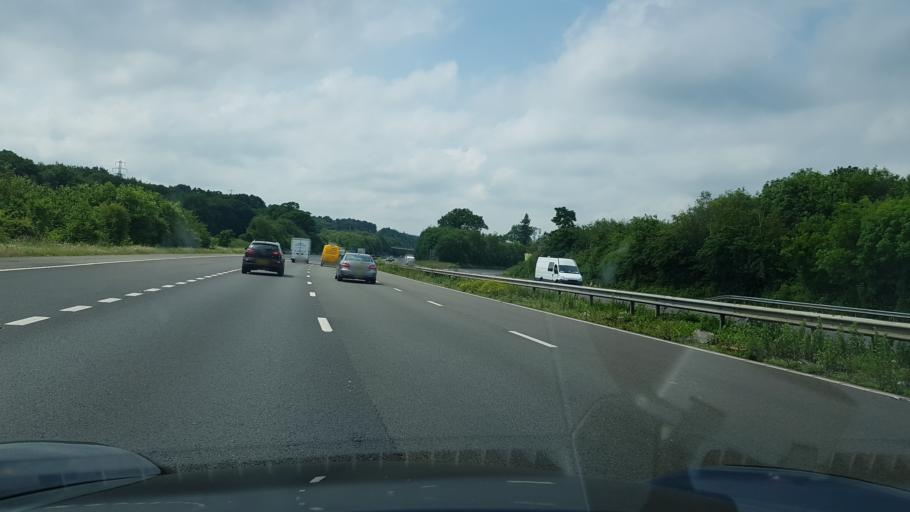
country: GB
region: England
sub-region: West Sussex
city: Maidenbower
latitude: 51.1082
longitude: -0.1398
